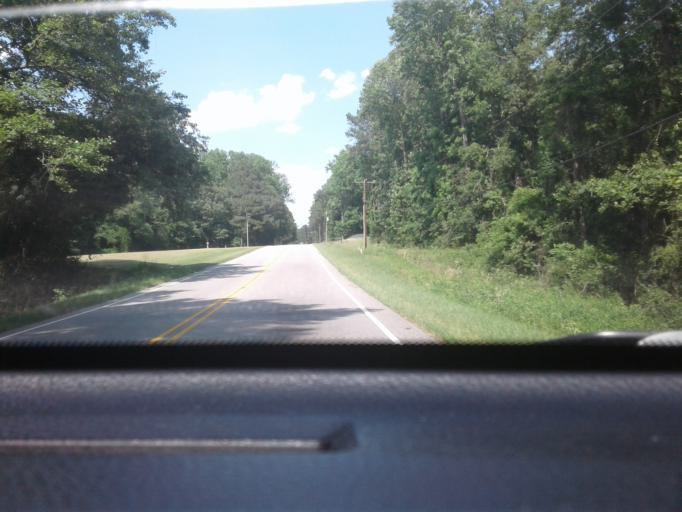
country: US
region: North Carolina
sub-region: Cumberland County
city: Eastover
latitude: 35.1814
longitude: -78.7082
